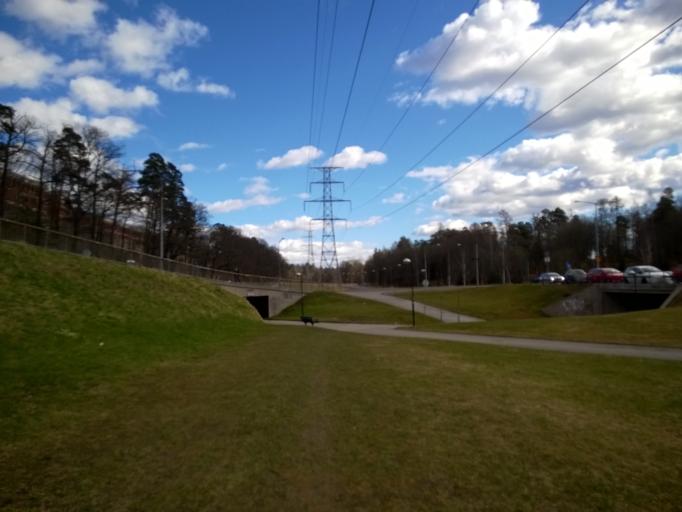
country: SE
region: Stockholm
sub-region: Norrtalje Kommun
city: Bergshamra
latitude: 59.3697
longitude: 18.0594
